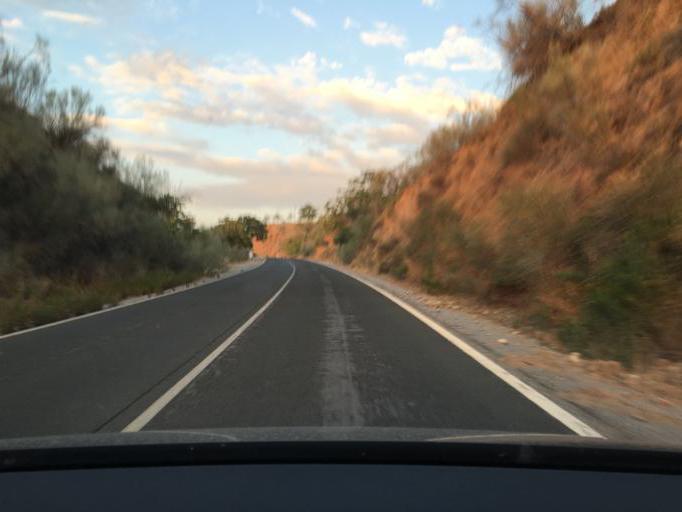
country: ES
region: Andalusia
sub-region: Provincia de Granada
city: Jun
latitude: 37.1977
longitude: -3.5729
